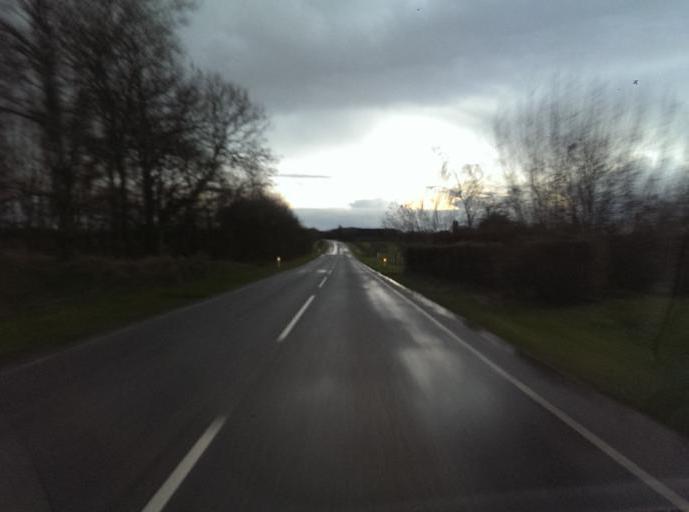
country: DK
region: South Denmark
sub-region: Esbjerg Kommune
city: Bramming
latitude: 55.4557
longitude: 8.6866
